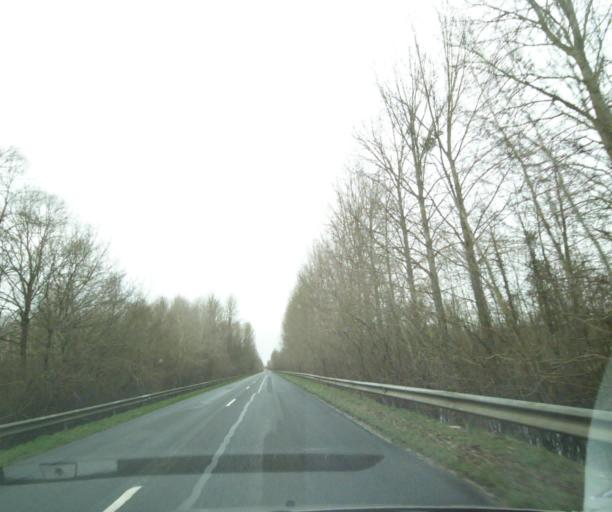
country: FR
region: Picardie
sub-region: Departement de l'Oise
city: Noyon
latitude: 49.5584
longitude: 3.0392
